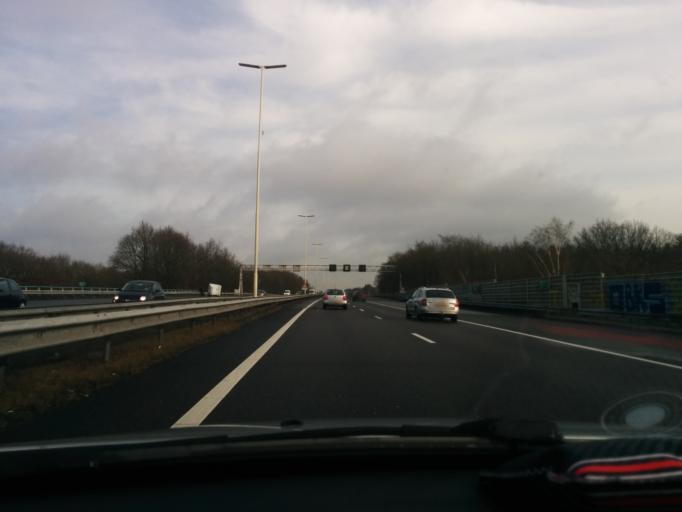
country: NL
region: North Holland
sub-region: Gemeente Hilversum
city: Hilversum
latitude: 52.1774
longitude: 5.1797
